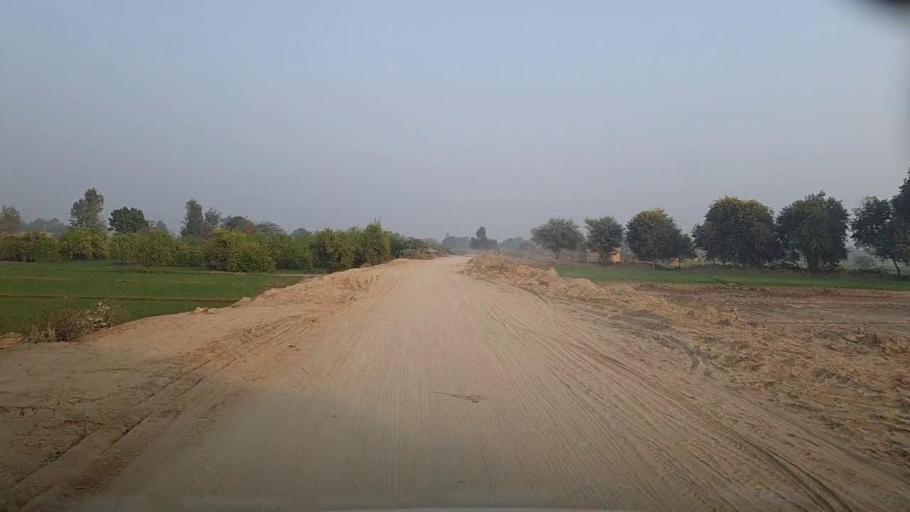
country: PK
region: Sindh
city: Bozdar
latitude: 27.0838
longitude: 68.5621
